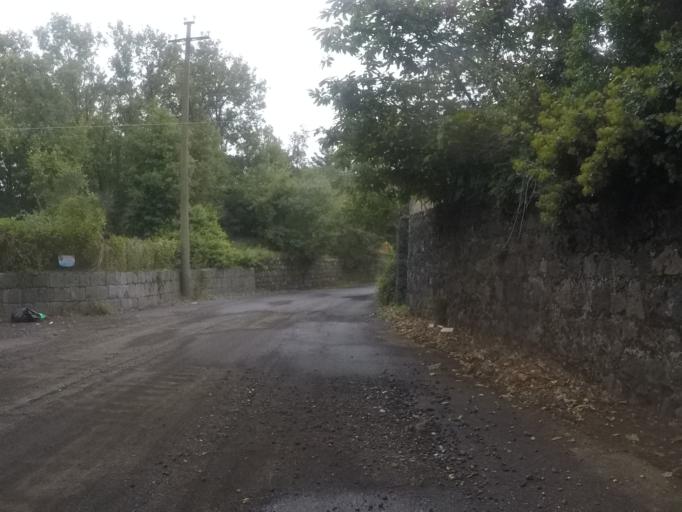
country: IT
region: Sicily
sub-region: Catania
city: Pedara
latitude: 37.6518
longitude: 15.0493
